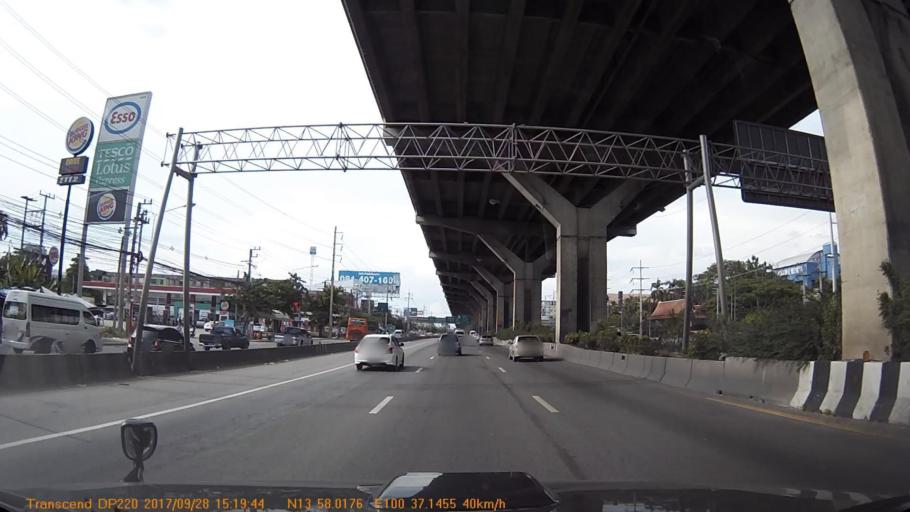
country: TH
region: Bangkok
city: Sai Mai
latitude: 13.9672
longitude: 100.6192
